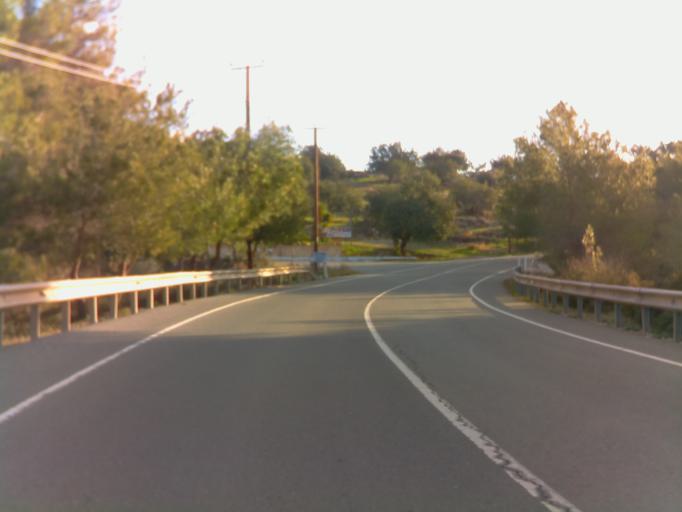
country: CY
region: Pafos
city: Pegeia
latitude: 34.8983
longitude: 32.3710
